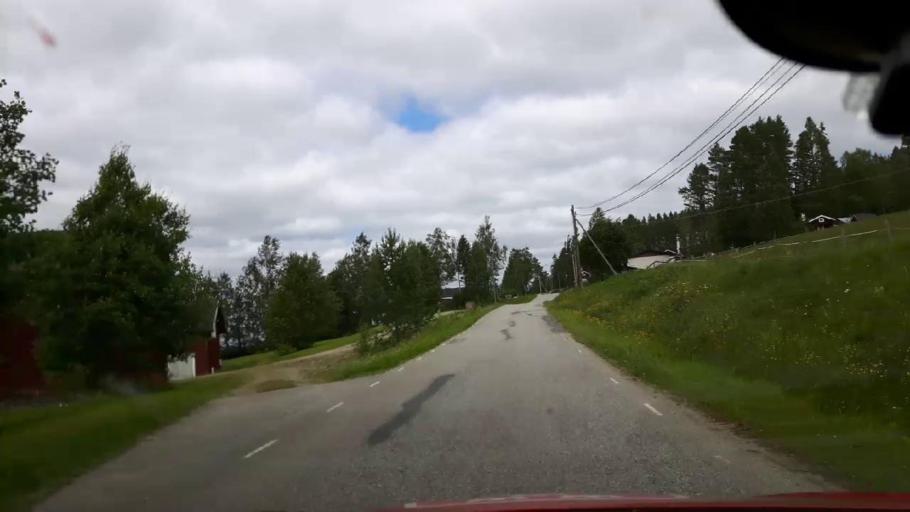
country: SE
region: Jaemtland
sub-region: Braecke Kommun
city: Braecke
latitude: 62.8674
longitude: 15.2717
